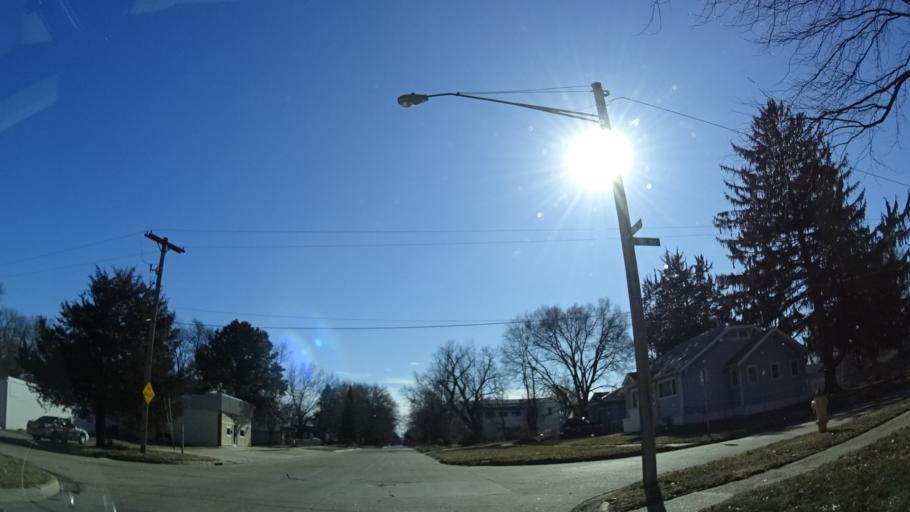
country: US
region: Nebraska
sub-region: Sarpy County
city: Bellevue
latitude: 41.1419
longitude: -95.8909
